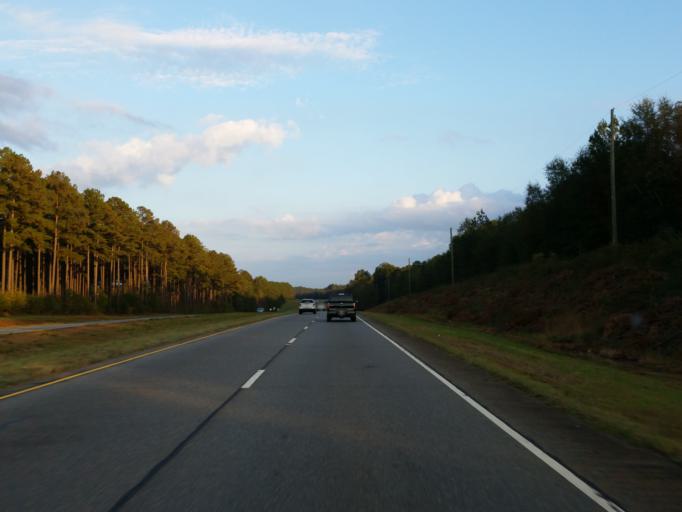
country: US
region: Georgia
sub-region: Houston County
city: Perry
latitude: 32.4152
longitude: -83.6877
